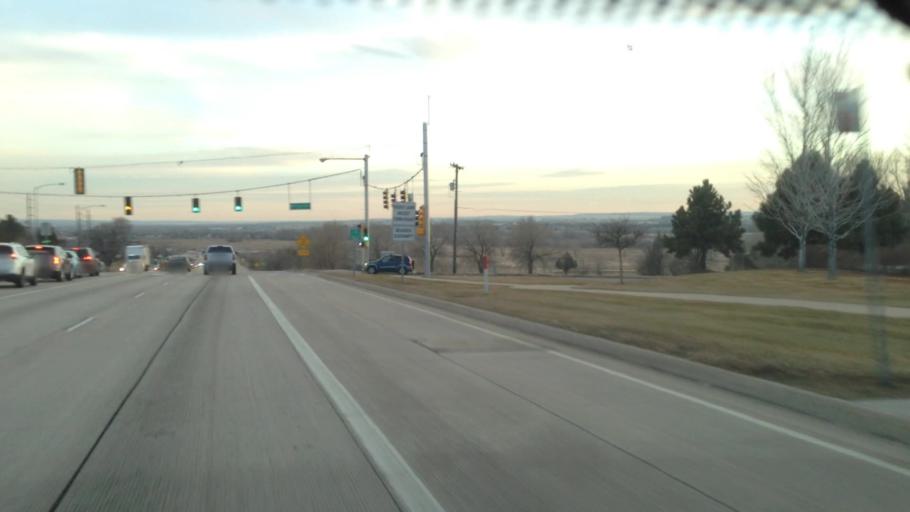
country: US
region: Colorado
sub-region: Arapahoe County
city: Dove Valley
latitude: 39.6246
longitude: -104.8220
